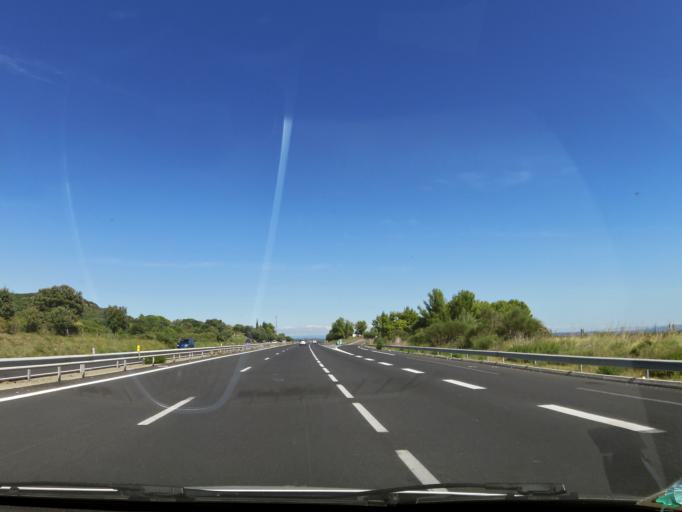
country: FR
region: Languedoc-Roussillon
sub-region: Departement du Gard
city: Ledenon
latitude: 43.9011
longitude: 4.5260
